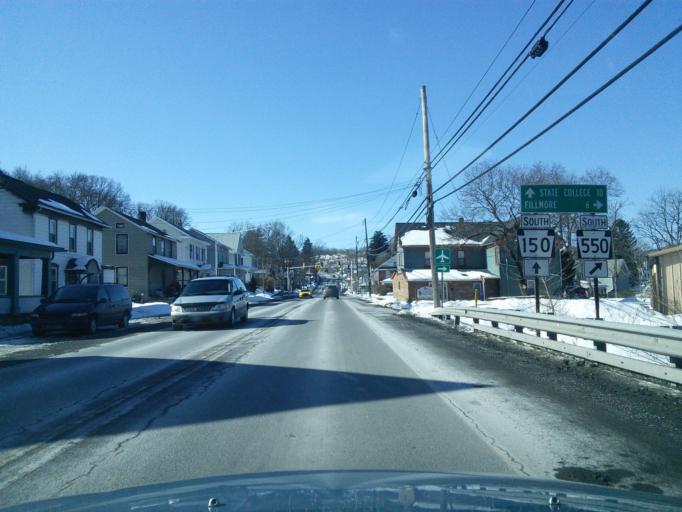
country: US
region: Pennsylvania
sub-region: Centre County
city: Bellefonte
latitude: 40.9059
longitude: -77.7852
